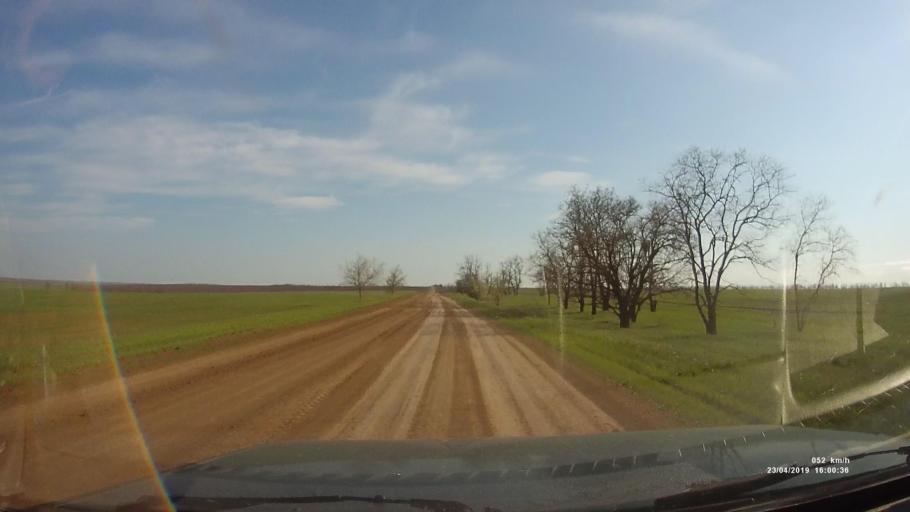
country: RU
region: Rostov
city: Remontnoye
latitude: 46.5082
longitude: 43.1067
